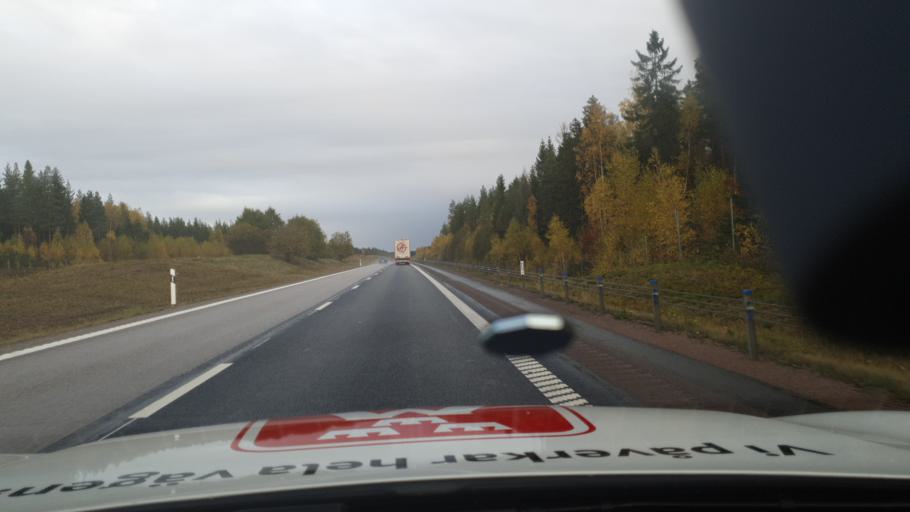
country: SE
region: Uppsala
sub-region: Tierps Kommun
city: Tierp
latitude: 60.2433
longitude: 17.5018
